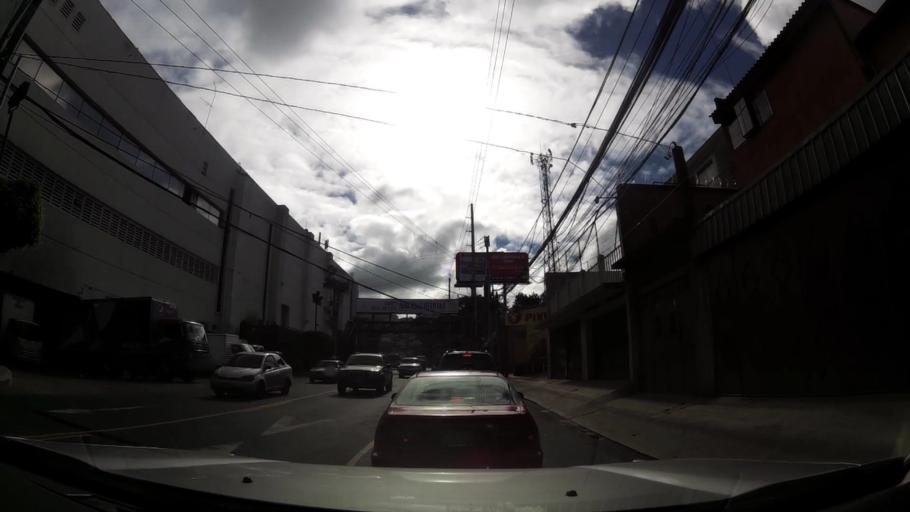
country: GT
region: Guatemala
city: Santa Catarina Pinula
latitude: 14.5797
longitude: -90.4962
